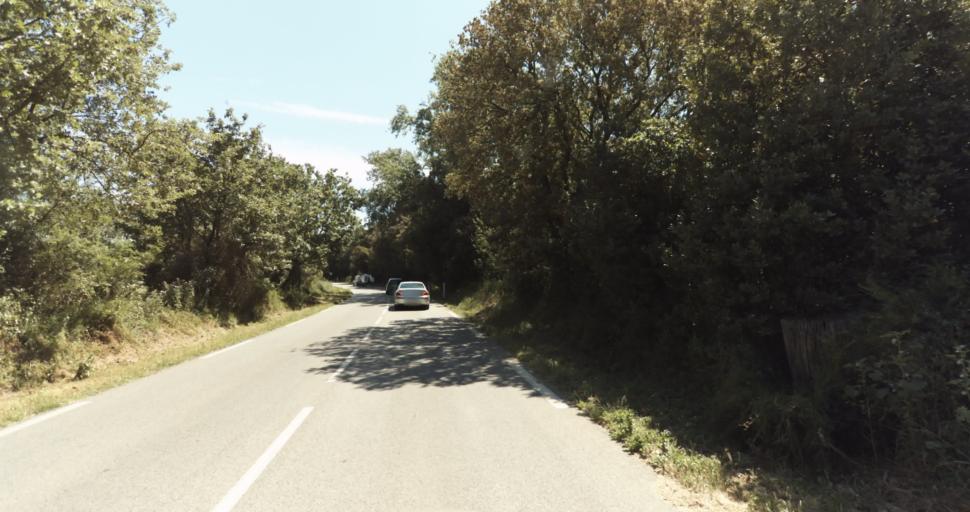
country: FR
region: Provence-Alpes-Cote d'Azur
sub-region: Departement du Var
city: Hyeres
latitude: 43.1357
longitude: 6.1576
